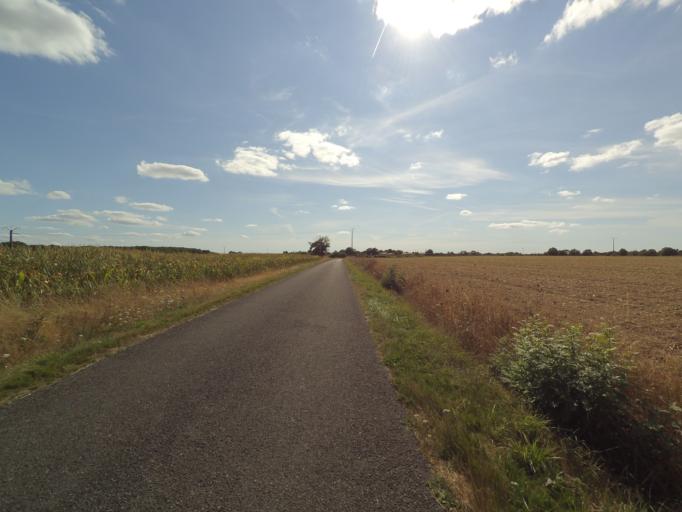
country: FR
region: Pays de la Loire
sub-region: Departement de la Loire-Atlantique
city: Vieillevigne
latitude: 46.9565
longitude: -1.4479
